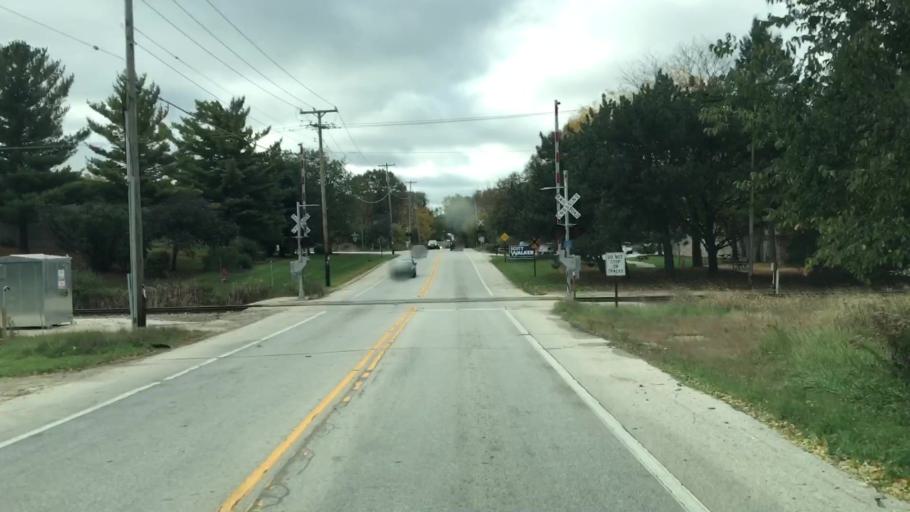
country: US
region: Wisconsin
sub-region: Waukesha County
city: Brookfield
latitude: 43.0694
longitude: -88.1260
